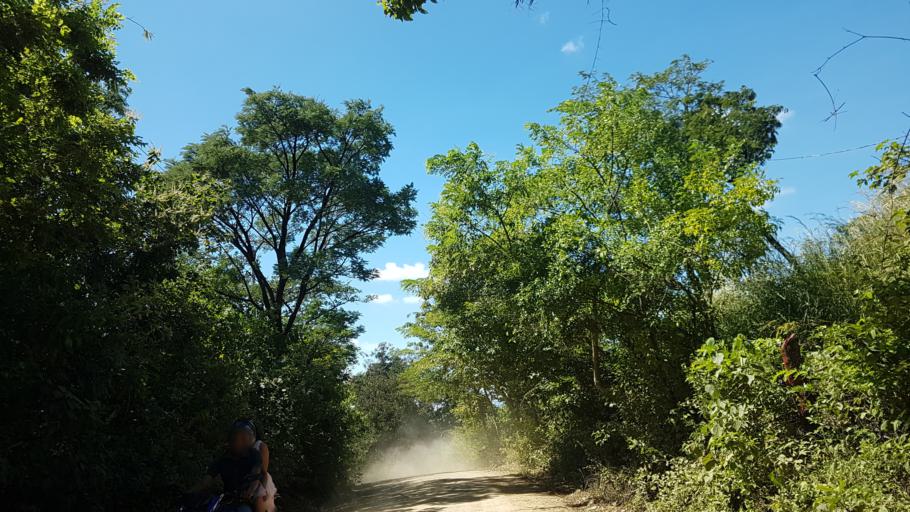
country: HN
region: El Paraiso
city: Santa Cruz
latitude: 13.7342
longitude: -86.6766
